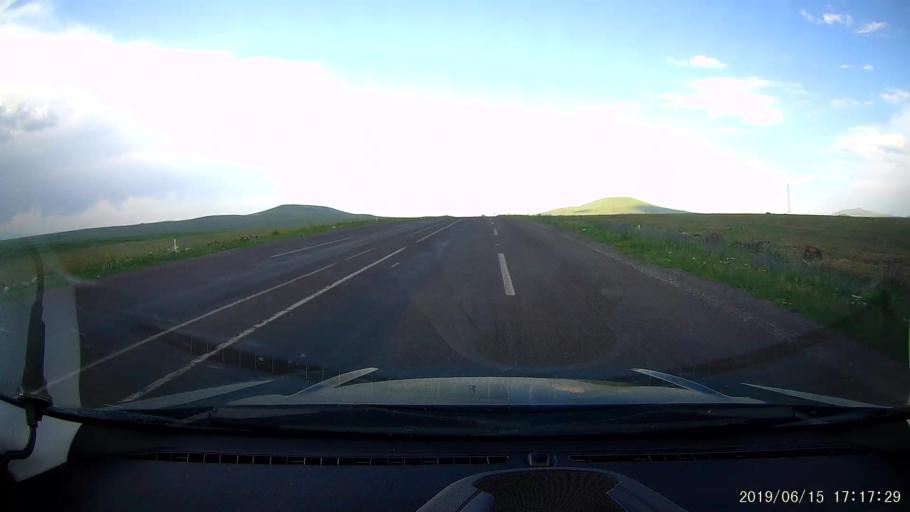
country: TR
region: Kars
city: Kars
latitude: 40.6147
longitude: 43.2395
